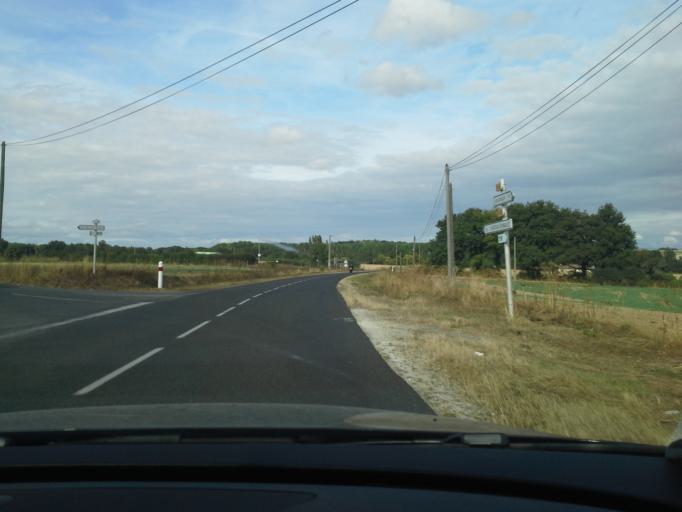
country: FR
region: Centre
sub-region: Departement d'Indre-et-Loire
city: Auzouer-en-Touraine
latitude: 47.5195
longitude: 0.9132
